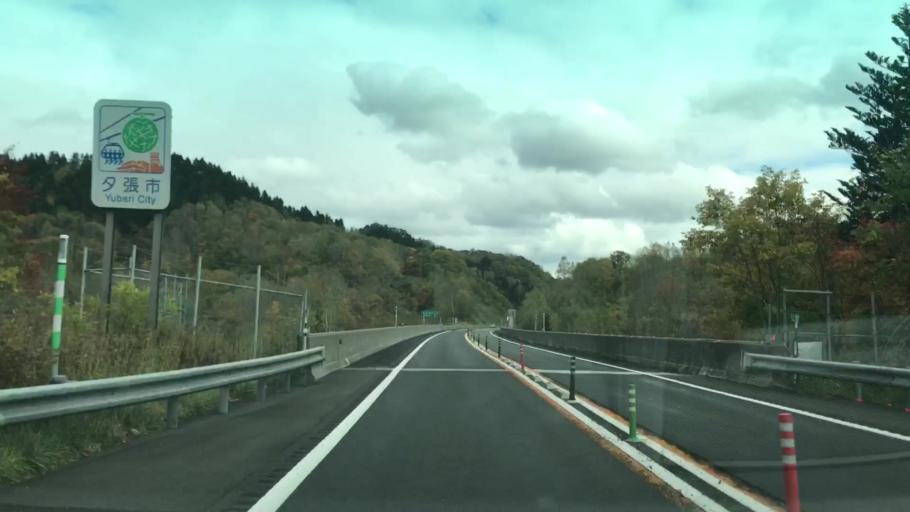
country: JP
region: Hokkaido
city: Chitose
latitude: 42.9157
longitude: 141.9656
